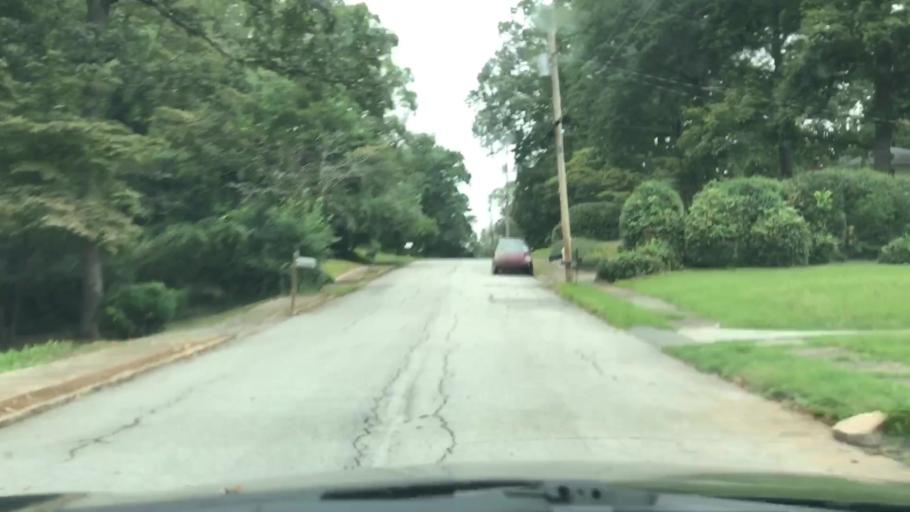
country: US
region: Georgia
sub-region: DeKalb County
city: Belvedere Park
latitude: 33.7589
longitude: -84.2717
